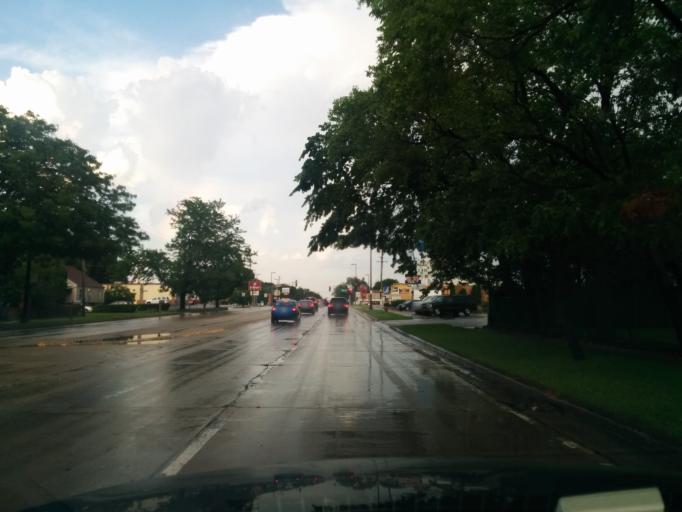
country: US
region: Illinois
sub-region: Cook County
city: Burbank
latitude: 41.7338
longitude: -87.7822
